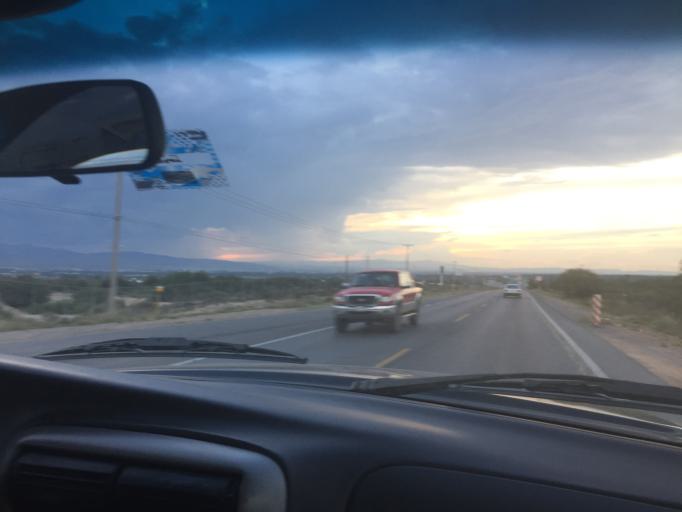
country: MX
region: San Luis Potosi
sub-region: San Luis Potosi
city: Ciudad Satelite
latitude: 22.1257
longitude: -100.8185
